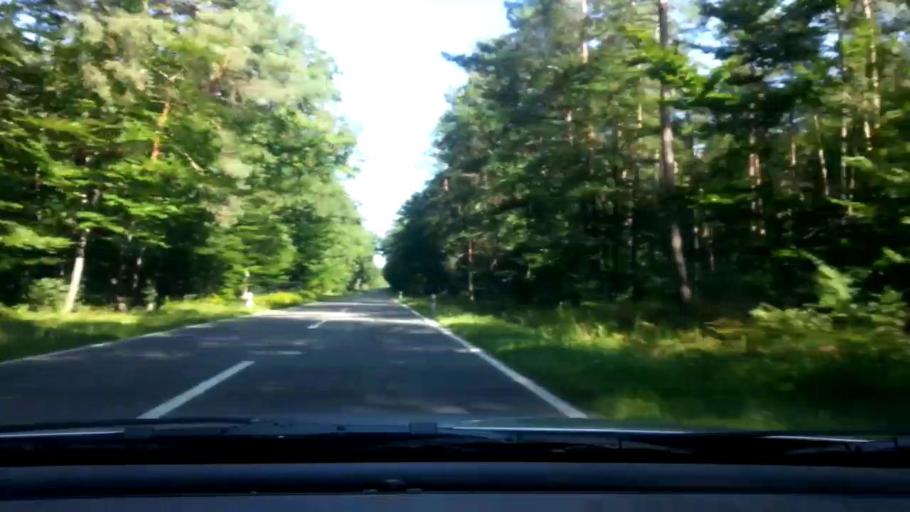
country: DE
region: Bavaria
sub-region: Upper Franconia
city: Strullendorf
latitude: 49.8592
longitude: 10.9578
